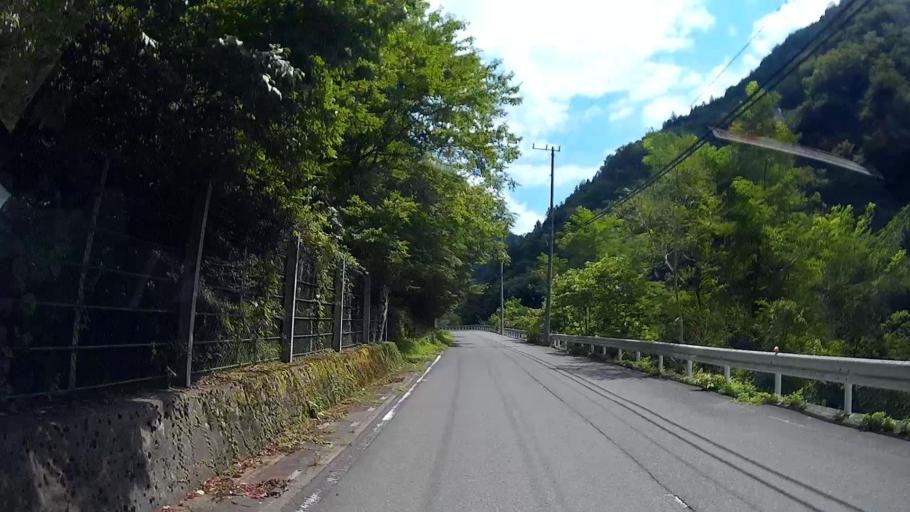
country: JP
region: Saitama
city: Chichibu
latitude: 35.9193
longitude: 139.0728
